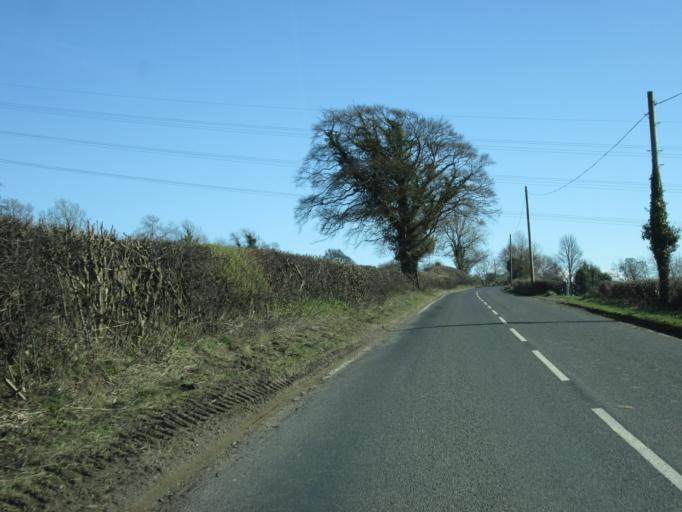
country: GB
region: England
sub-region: Northumberland
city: Wall
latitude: 55.0110
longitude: -2.1302
